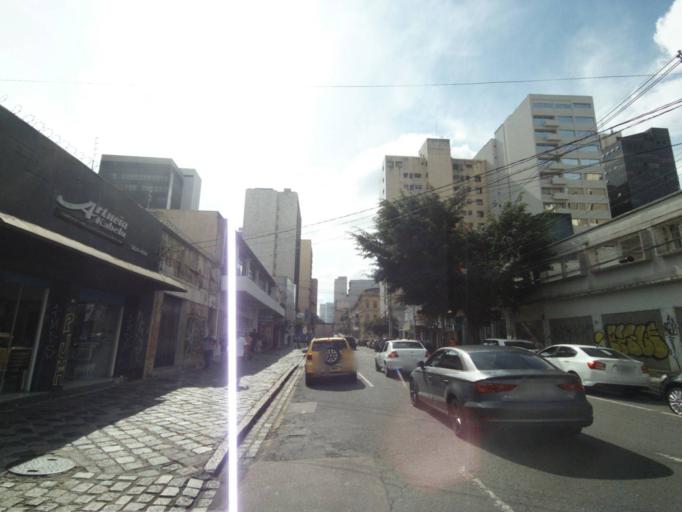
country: BR
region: Parana
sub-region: Curitiba
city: Curitiba
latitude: -25.4304
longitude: -49.2648
